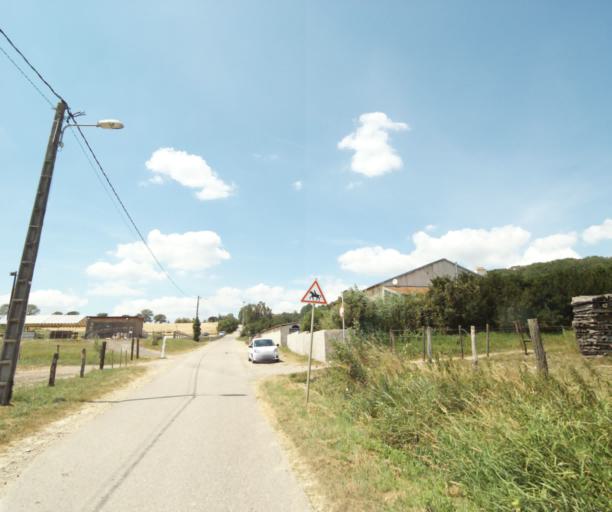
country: FR
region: Lorraine
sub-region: Departement de Meurthe-et-Moselle
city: Luneville
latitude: 48.6022
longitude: 6.4618
